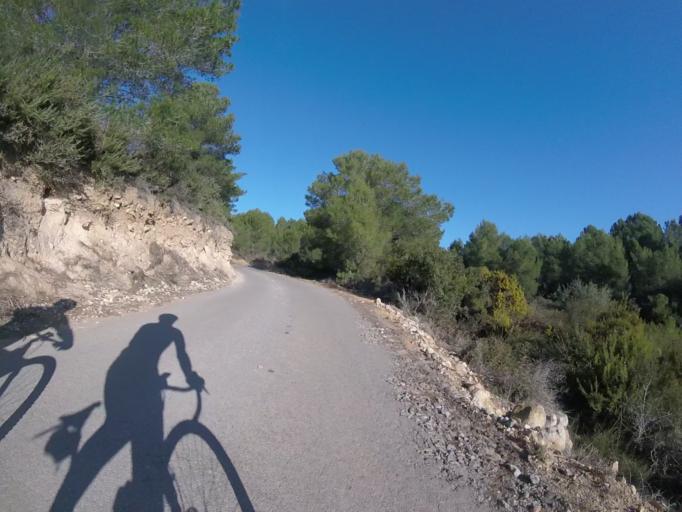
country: ES
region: Valencia
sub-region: Provincia de Castello
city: Alcala de Xivert
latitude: 40.2724
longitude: 0.2064
